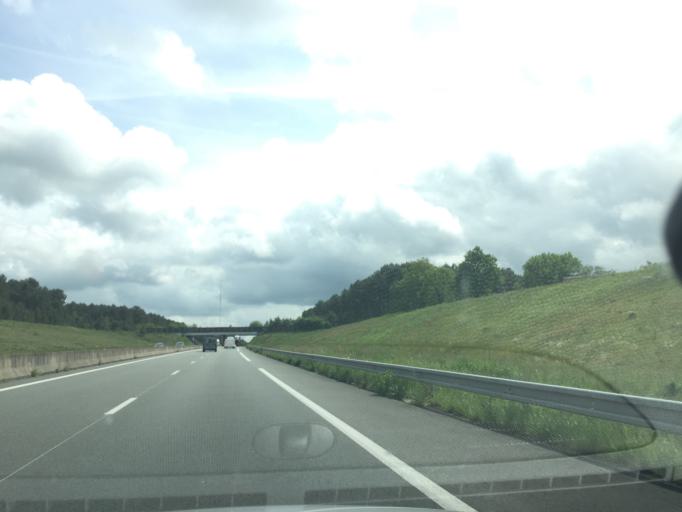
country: FR
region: Pays de la Loire
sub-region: Departement de la Sarthe
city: Mayet
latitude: 47.7870
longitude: 0.3071
